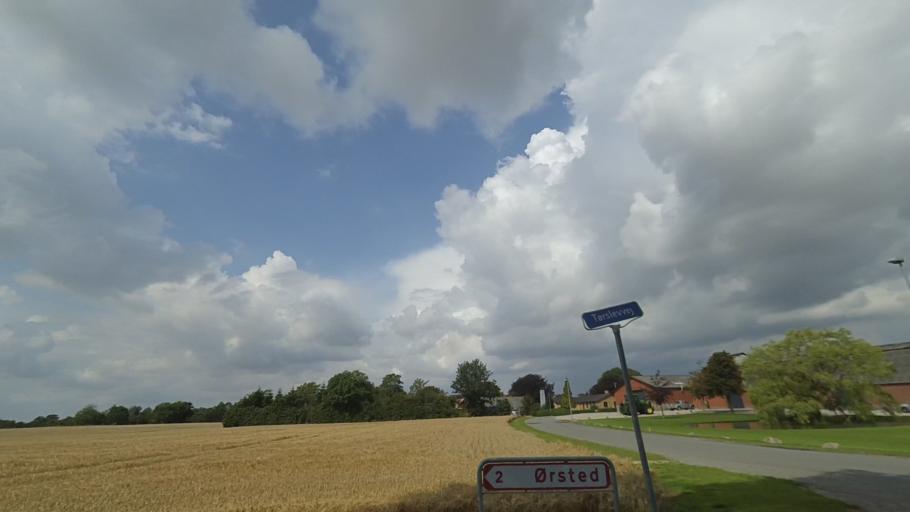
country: DK
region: Central Jutland
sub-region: Norddjurs Kommune
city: Allingabro
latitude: 56.5289
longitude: 10.3408
